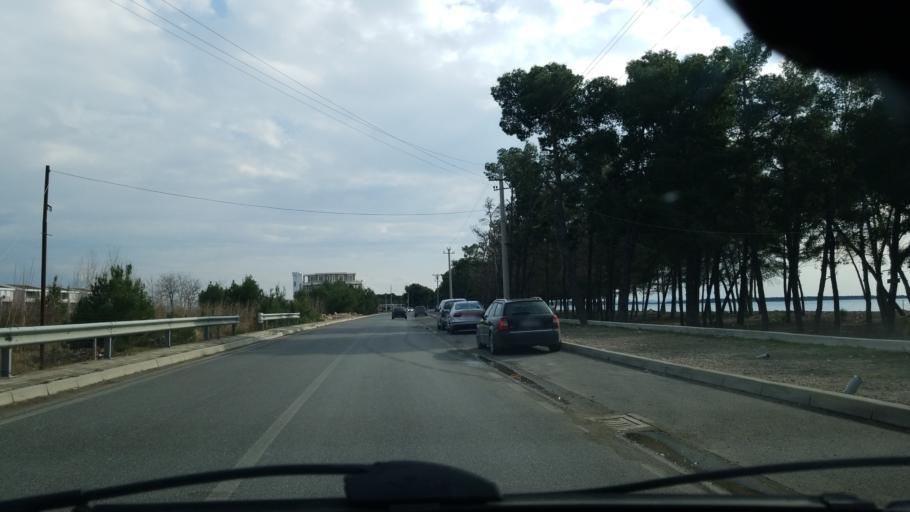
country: AL
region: Lezhe
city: Shengjin
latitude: 41.7919
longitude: 19.6029
